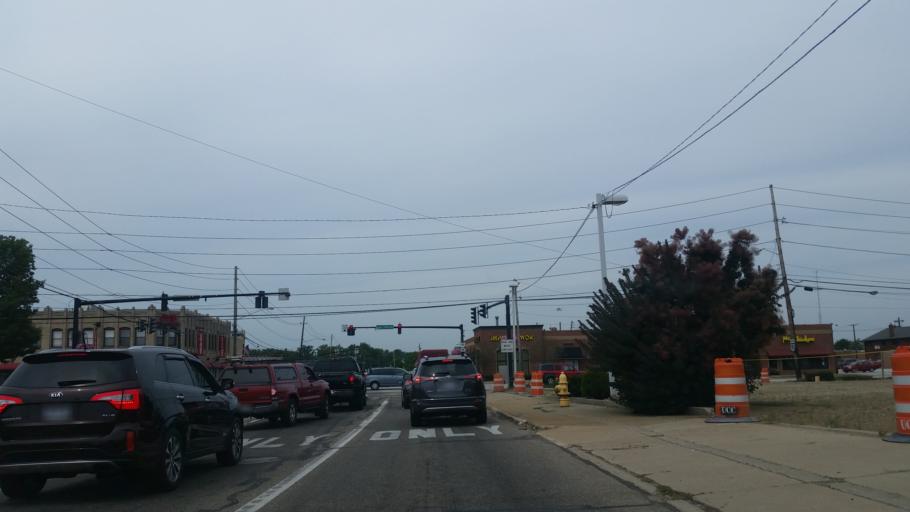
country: US
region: Ohio
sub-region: Cuyahoga County
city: Solon
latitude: 41.3851
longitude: -81.4369
